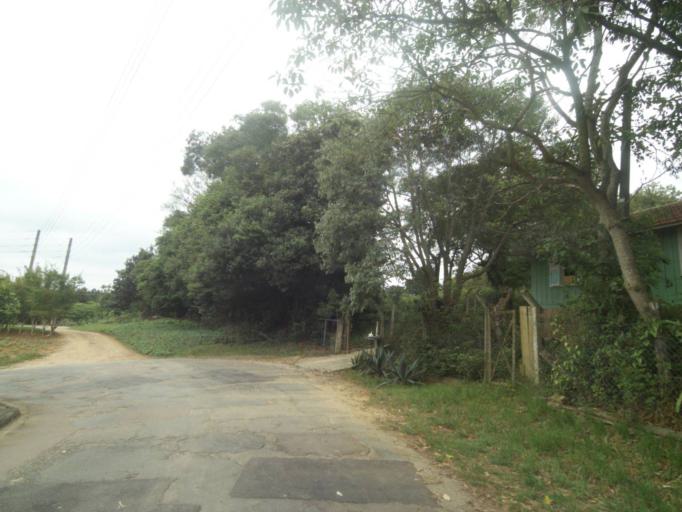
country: BR
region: Parana
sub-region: Curitiba
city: Curitiba
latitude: -25.3951
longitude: -49.2816
